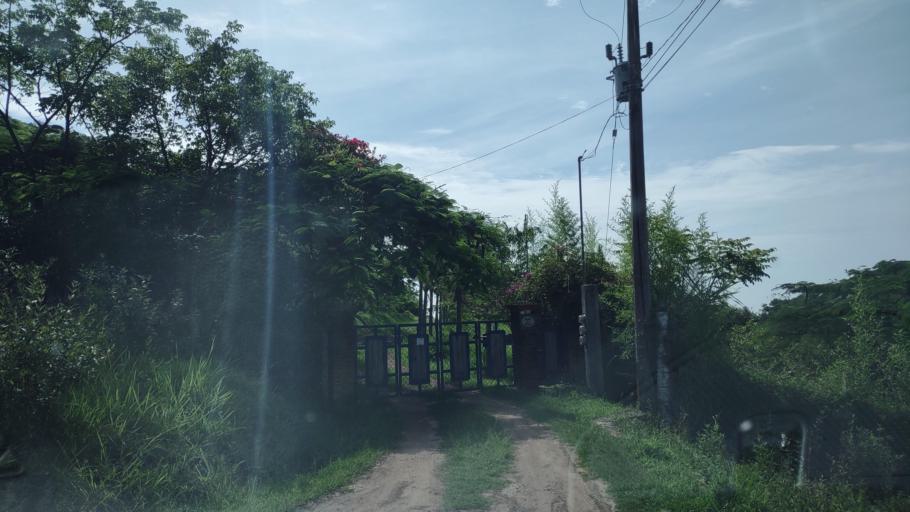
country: MX
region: Veracruz
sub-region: Emiliano Zapata
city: Dos Rios
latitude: 19.4712
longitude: -96.8252
